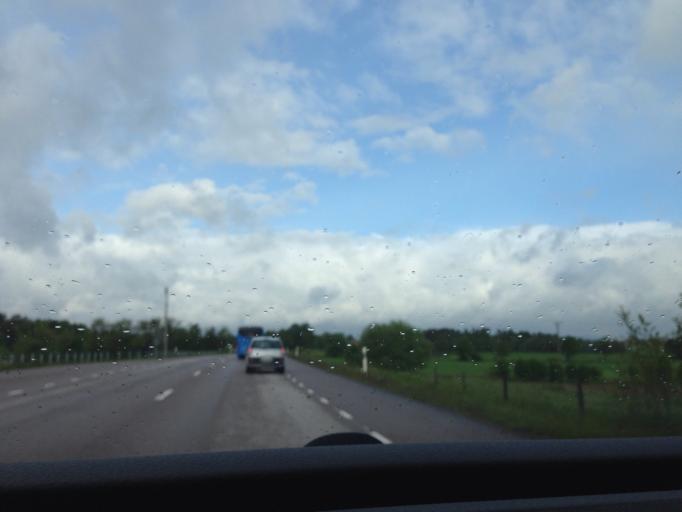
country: SE
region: Vaestra Goetaland
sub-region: Tibro Kommun
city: Tibro
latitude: 58.4096
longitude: 14.0279
